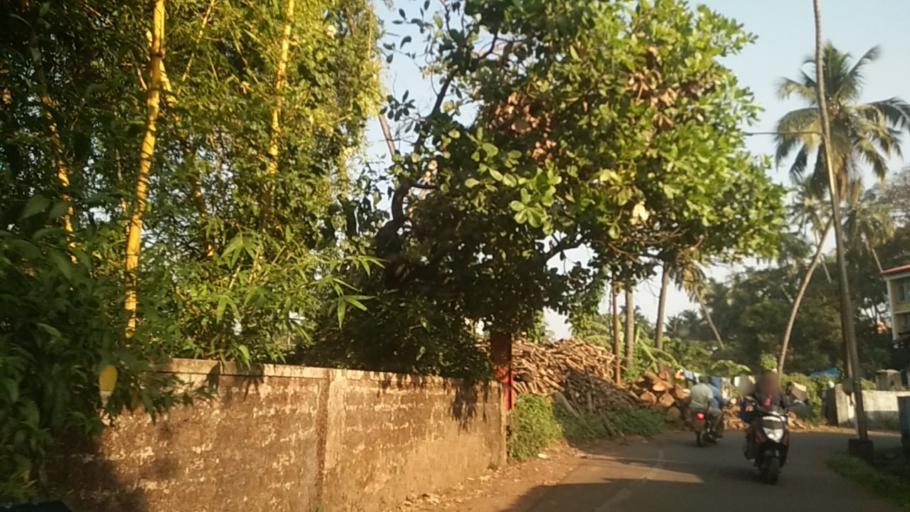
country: IN
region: Goa
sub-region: South Goa
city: Madgaon
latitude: 15.2816
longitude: 73.9562
